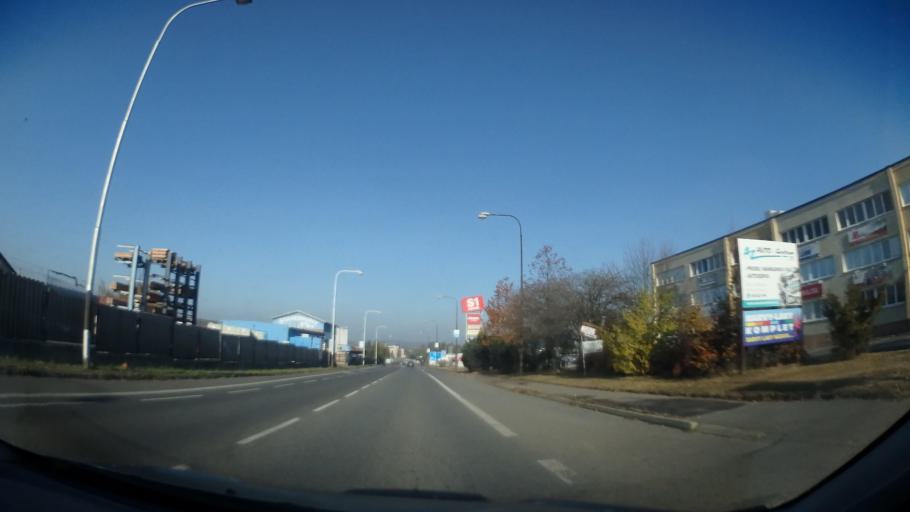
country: CZ
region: Vysocina
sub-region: Okres Zd'ar nad Sazavou
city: Zd'ar nad Sazavou
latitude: 49.5547
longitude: 15.9507
